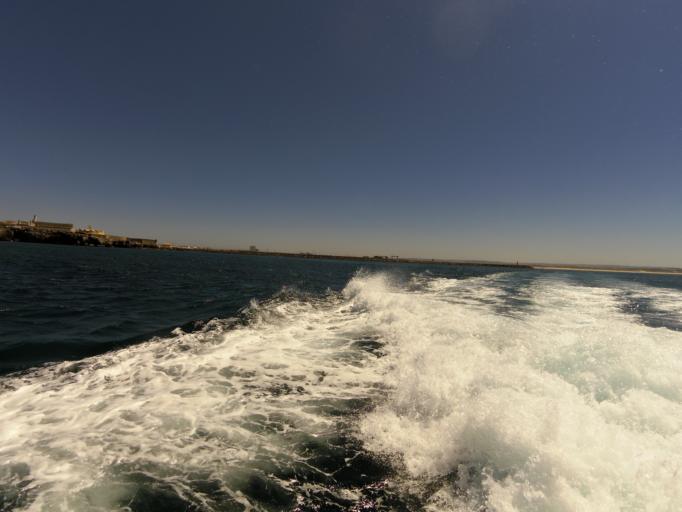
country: PT
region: Leiria
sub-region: Peniche
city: Peniche
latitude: 39.3491
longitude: -9.3841
